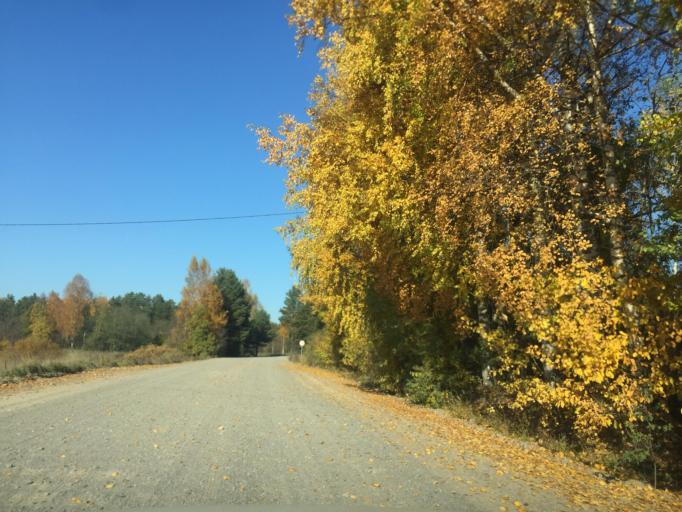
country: RU
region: Leningrad
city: Kuznechnoye
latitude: 61.3202
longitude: 29.9467
